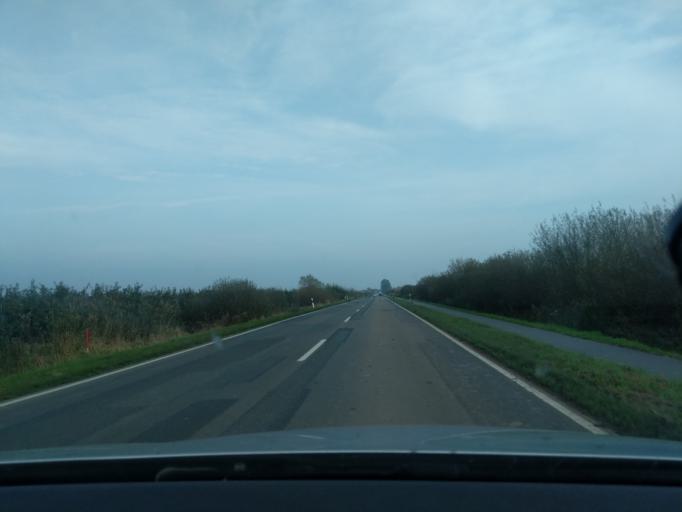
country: DE
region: Lower Saxony
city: Guderhandviertel
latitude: 53.5453
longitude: 9.5889
